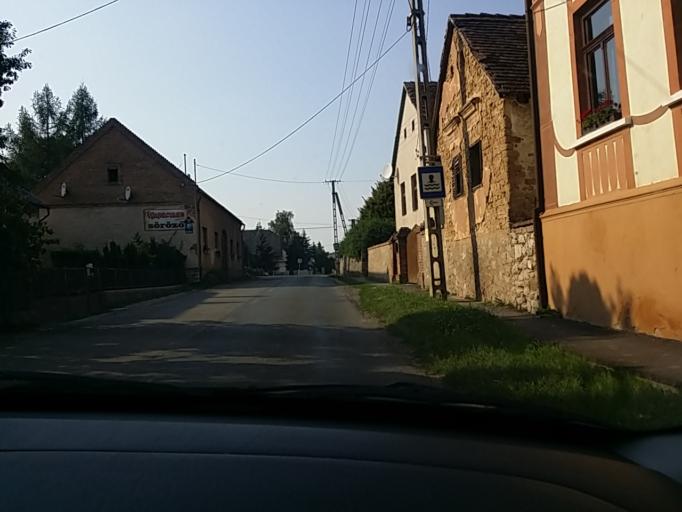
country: HU
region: Baranya
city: Pellerd
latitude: 46.1388
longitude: 18.1188
